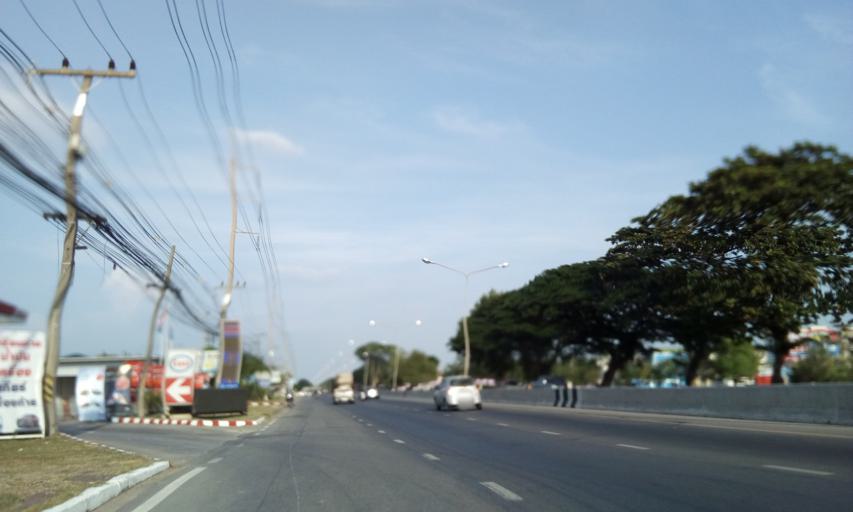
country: TH
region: Pathum Thani
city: Nong Suea
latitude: 14.0617
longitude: 100.8493
